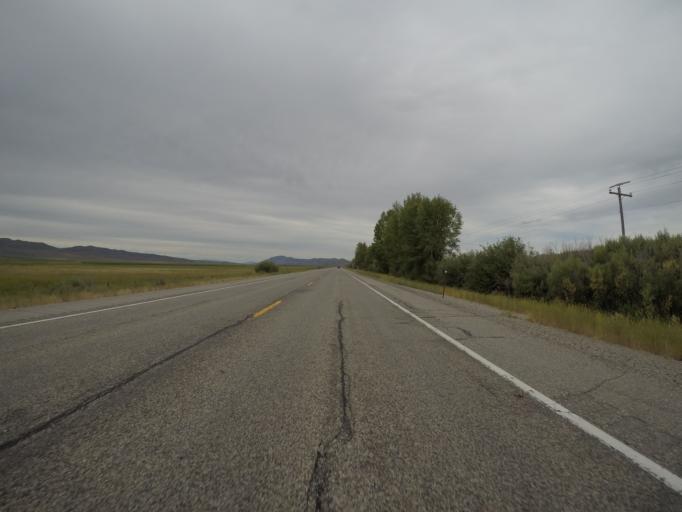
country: US
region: Utah
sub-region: Rich County
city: Randolph
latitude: 42.0038
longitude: -110.9372
